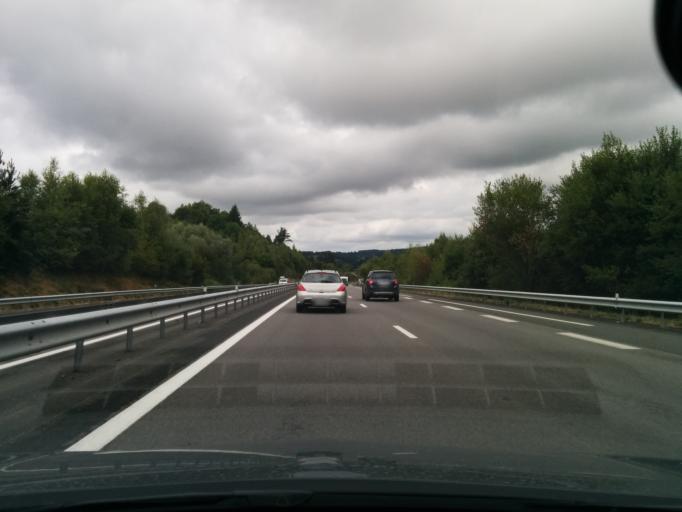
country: FR
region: Limousin
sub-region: Departement de la Correze
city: Vigeois
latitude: 45.3230
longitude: 1.5726
